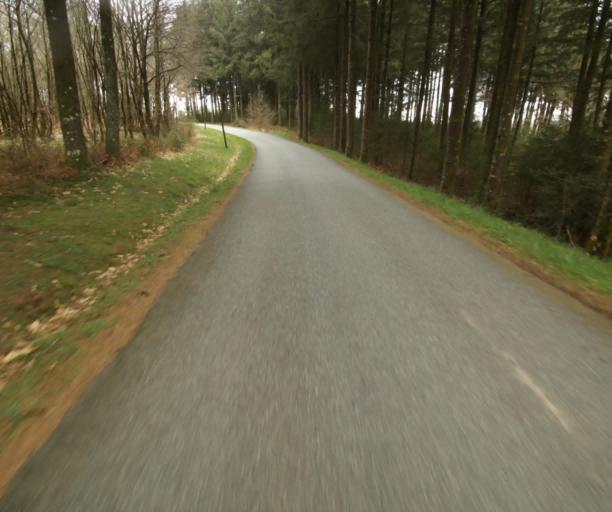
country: FR
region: Limousin
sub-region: Departement de la Correze
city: Correze
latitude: 45.3214
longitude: 1.9187
